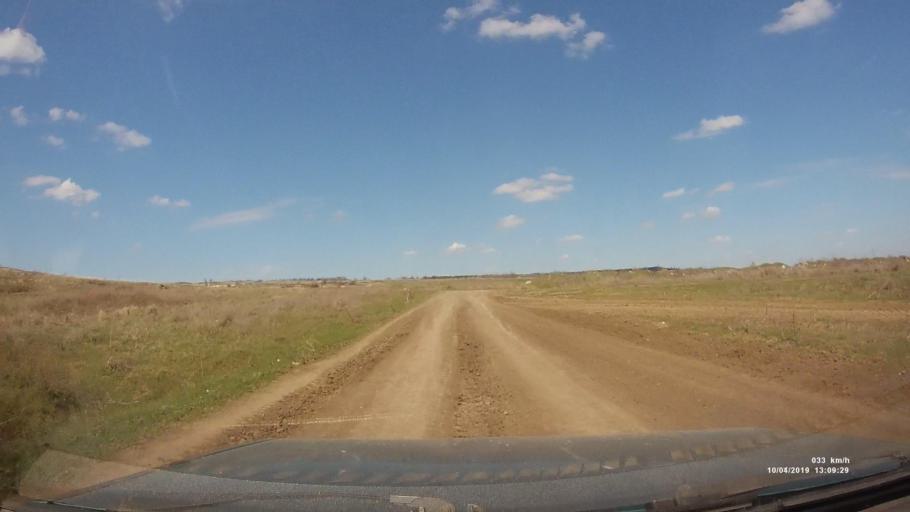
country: RU
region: Rostov
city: Masalovka
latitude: 48.4062
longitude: 40.2437
